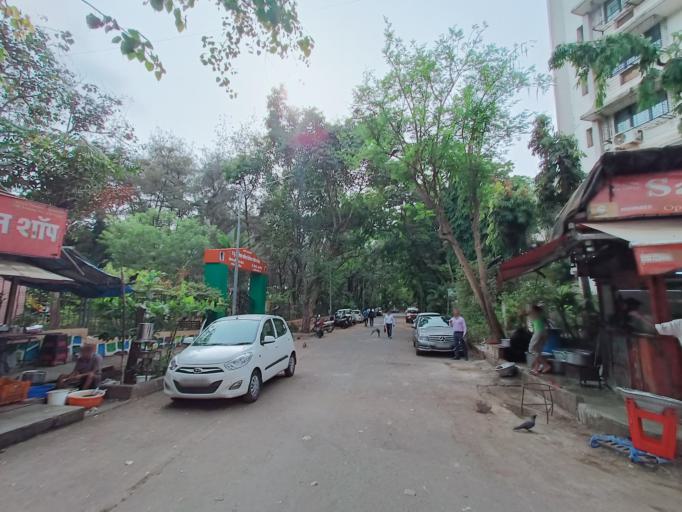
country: IN
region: Maharashtra
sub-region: Mumbai Suburban
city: Mumbai
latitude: 19.1119
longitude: 72.8299
